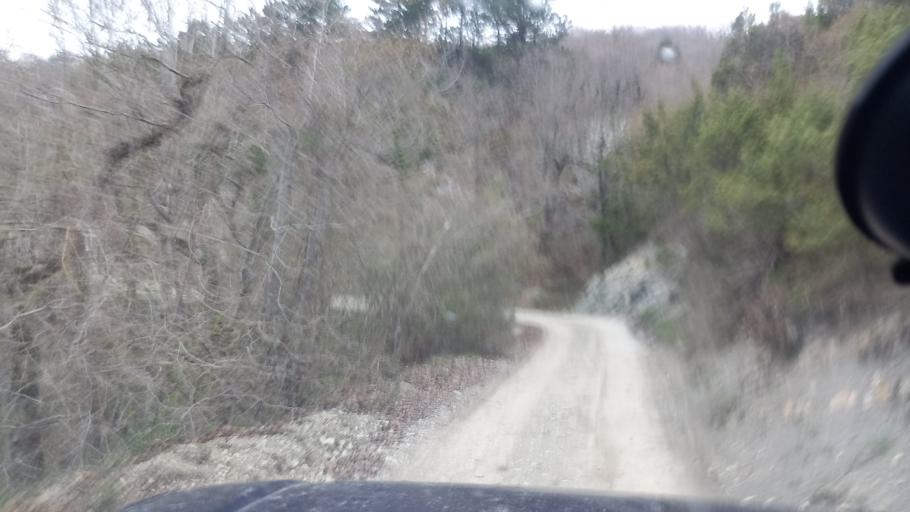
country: RU
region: Krasnodarskiy
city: Dzhubga
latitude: 44.3221
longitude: 38.6824
